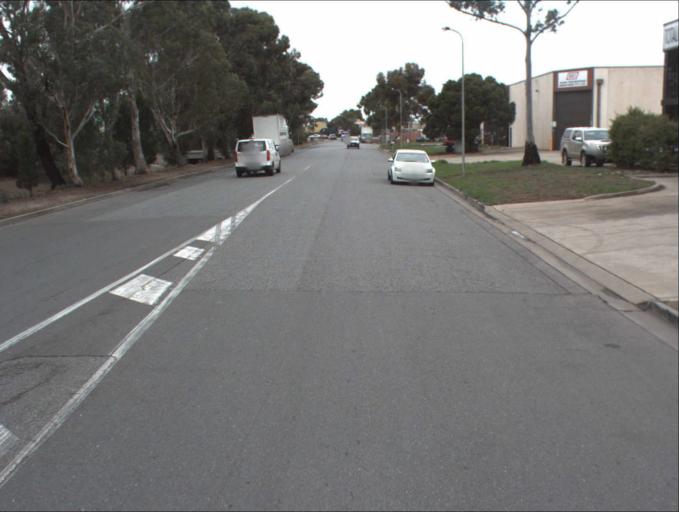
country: AU
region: South Australia
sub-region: Port Adelaide Enfield
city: Blair Athol
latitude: -34.8471
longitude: 138.5689
